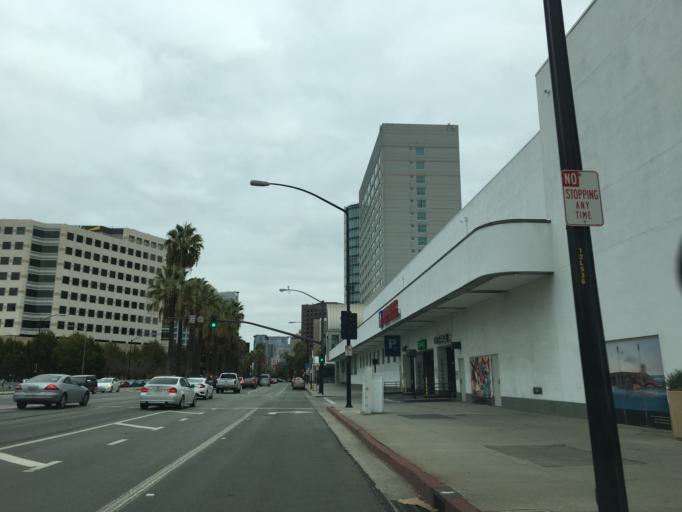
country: US
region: California
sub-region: Santa Clara County
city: San Jose
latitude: 37.3278
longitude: -121.8899
